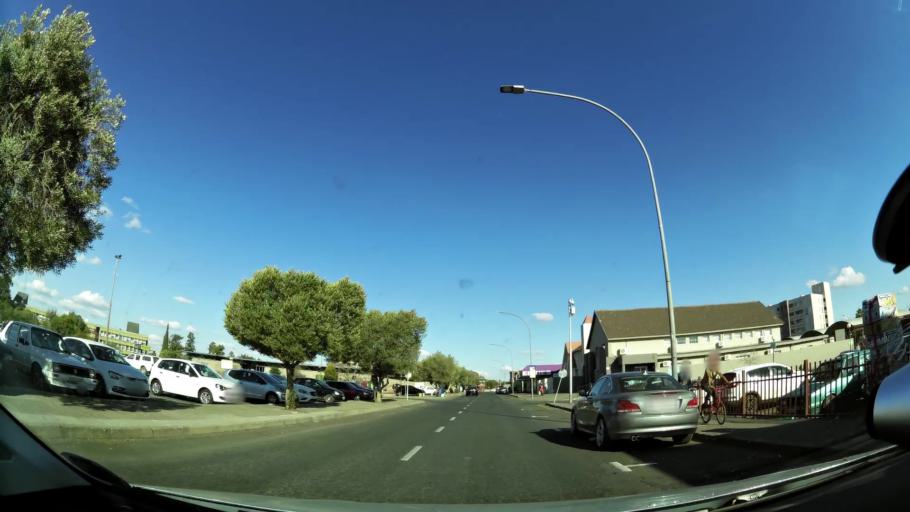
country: ZA
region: Northern Cape
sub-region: Frances Baard District Municipality
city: Kimberley
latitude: -28.7446
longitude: 24.7644
